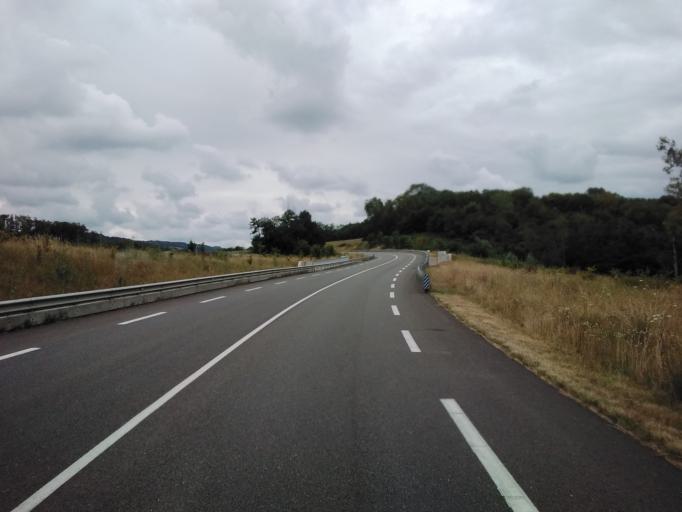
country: FR
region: Franche-Comte
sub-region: Departement du Jura
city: Montmorot
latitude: 46.6576
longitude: 5.5080
